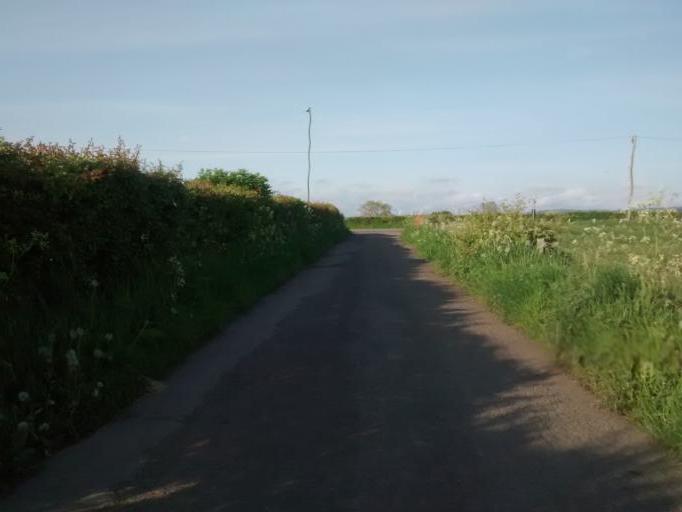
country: GB
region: England
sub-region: County Durham
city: Coxhoe
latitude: 54.7461
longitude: -1.5348
